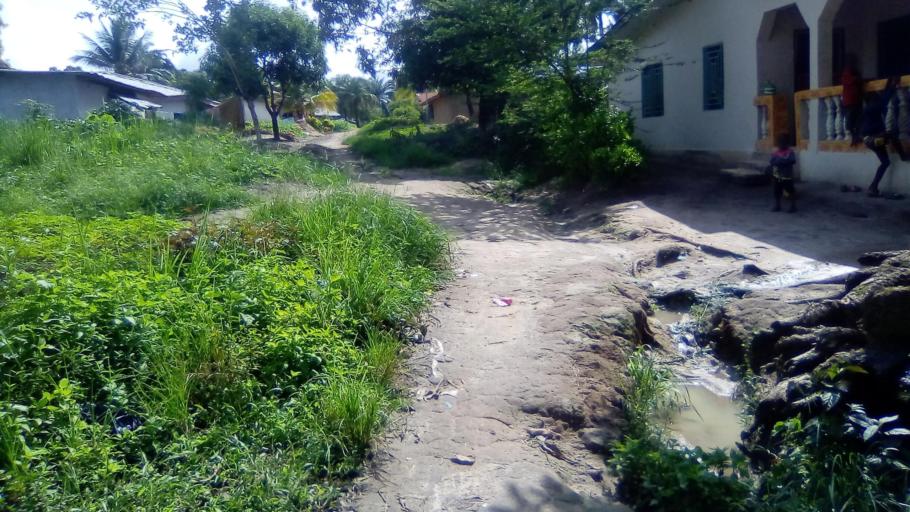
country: SL
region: Southern Province
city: Bo
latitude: 7.9748
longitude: -11.7265
